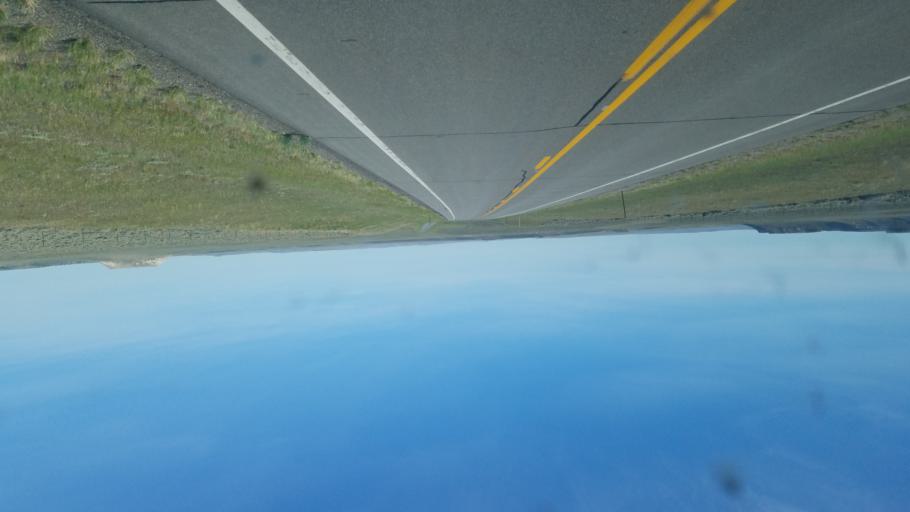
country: US
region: Wyoming
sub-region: Fremont County
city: Riverton
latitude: 42.6601
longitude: -108.1855
